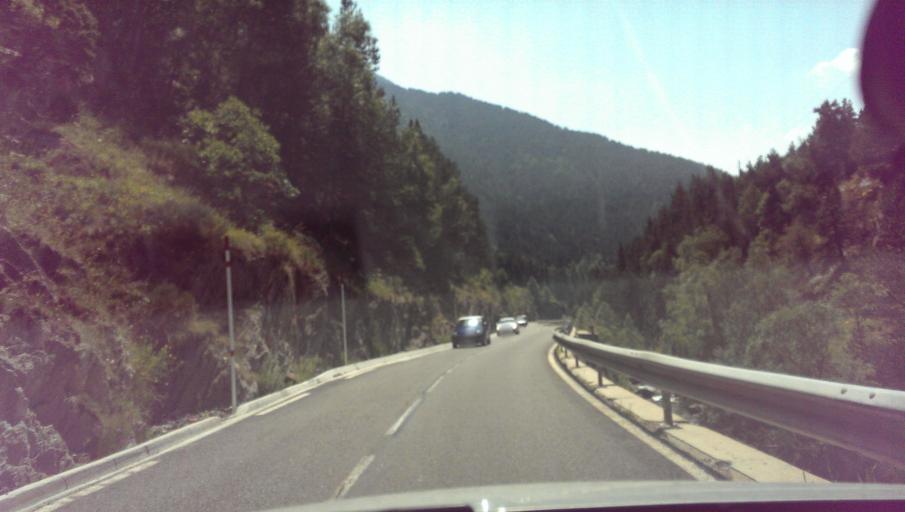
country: AD
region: Encamp
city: Pas de la Casa
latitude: 42.5439
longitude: 1.8264
